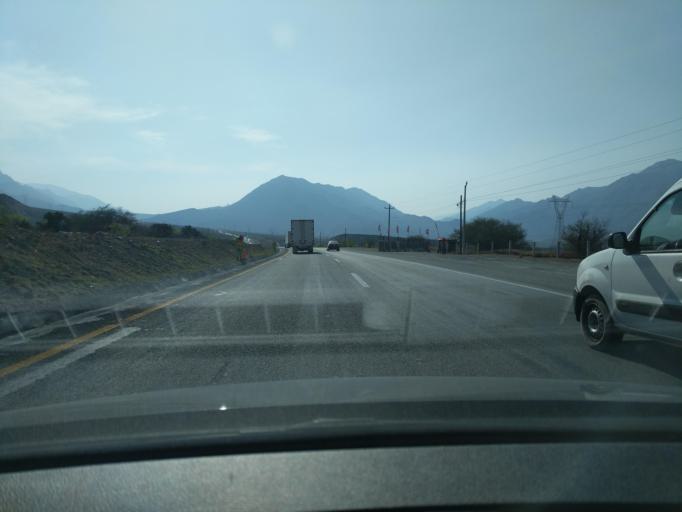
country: MX
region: Nuevo Leon
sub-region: Garcia
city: Las Torres de Guadalupe
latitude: 25.6749
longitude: -100.6825
